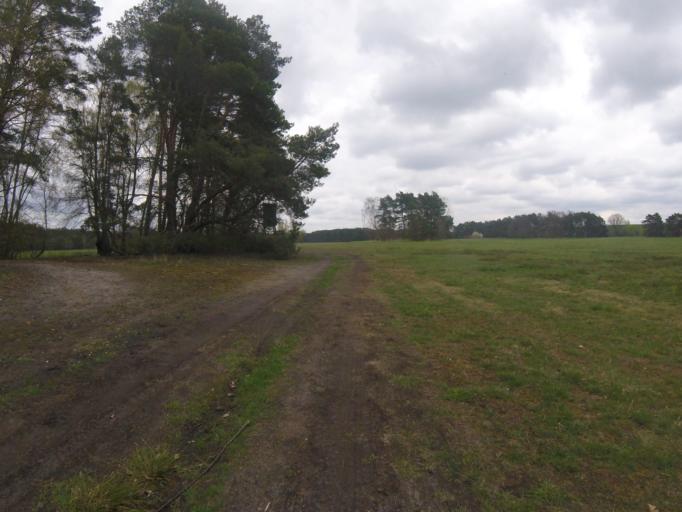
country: DE
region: Brandenburg
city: Mittenwalde
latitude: 52.2637
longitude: 13.5895
